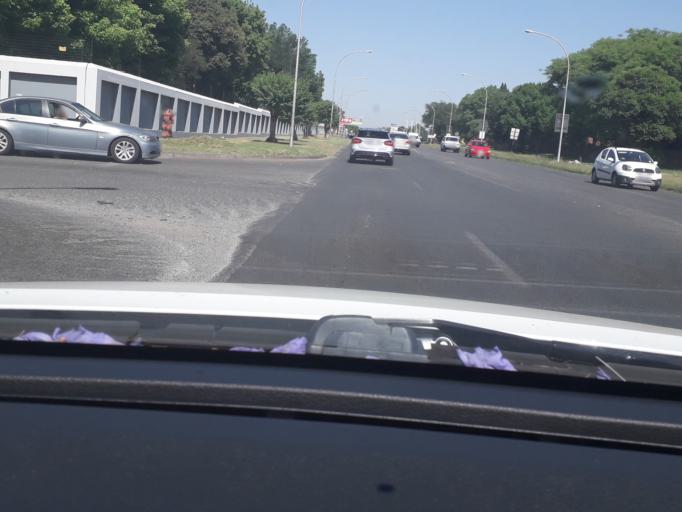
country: ZA
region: Gauteng
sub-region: Ekurhuleni Metropolitan Municipality
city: Benoni
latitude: -26.1794
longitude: 28.2841
